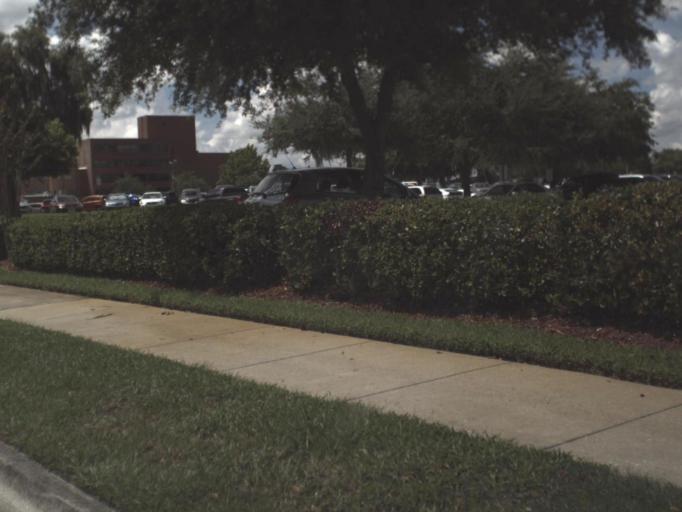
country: US
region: Florida
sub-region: Polk County
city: Lakeland
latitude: 28.0690
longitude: -81.9534
